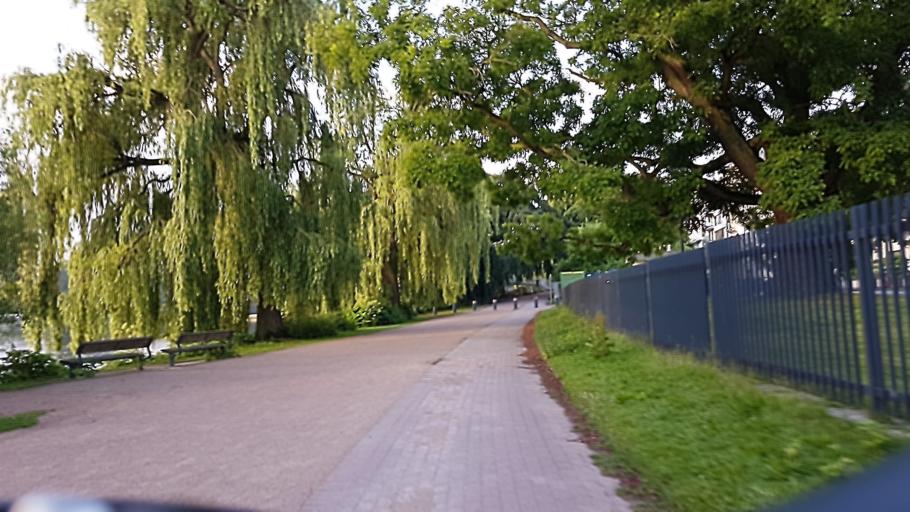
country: DE
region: Hamburg
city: Altstadt
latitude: 53.5620
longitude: 9.9976
